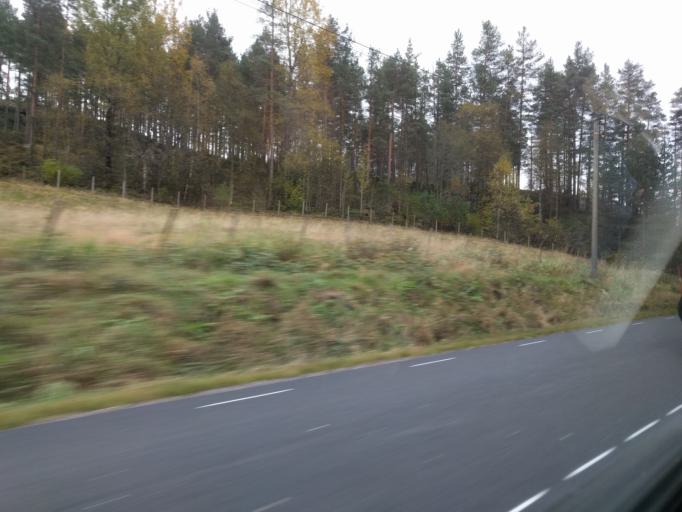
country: NO
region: Aust-Agder
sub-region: Iveland
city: Birketveit
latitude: 58.4396
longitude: 7.7882
